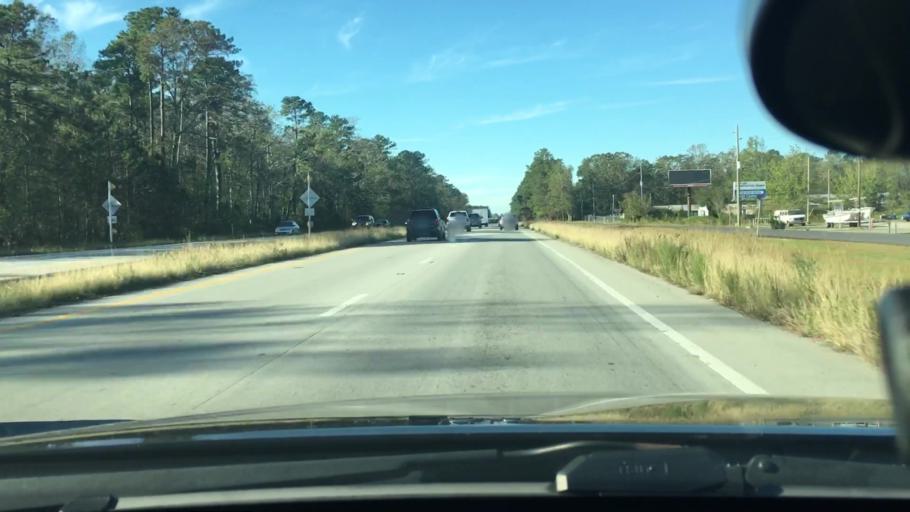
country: US
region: North Carolina
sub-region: Craven County
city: James City
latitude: 35.0388
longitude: -77.0076
